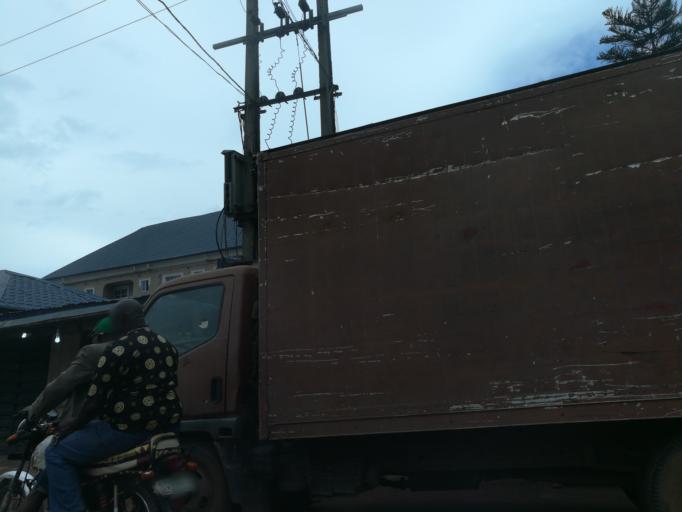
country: NG
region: Lagos
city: Agege
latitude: 6.6088
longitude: 3.3188
